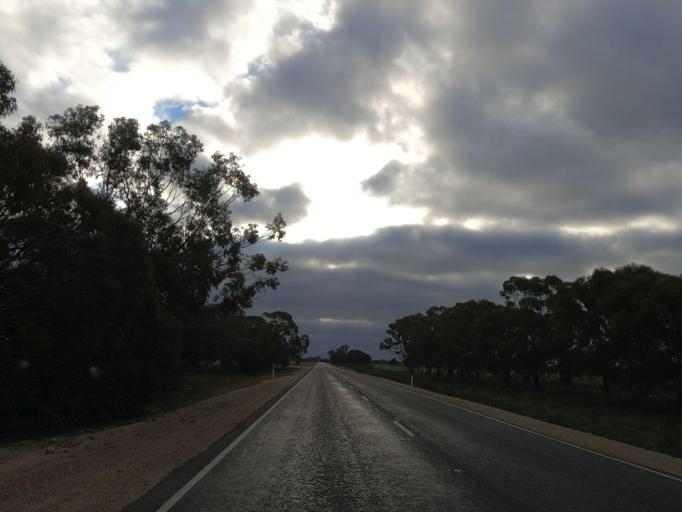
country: AU
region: Victoria
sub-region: Swan Hill
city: Swan Hill
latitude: -35.6566
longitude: 143.8518
